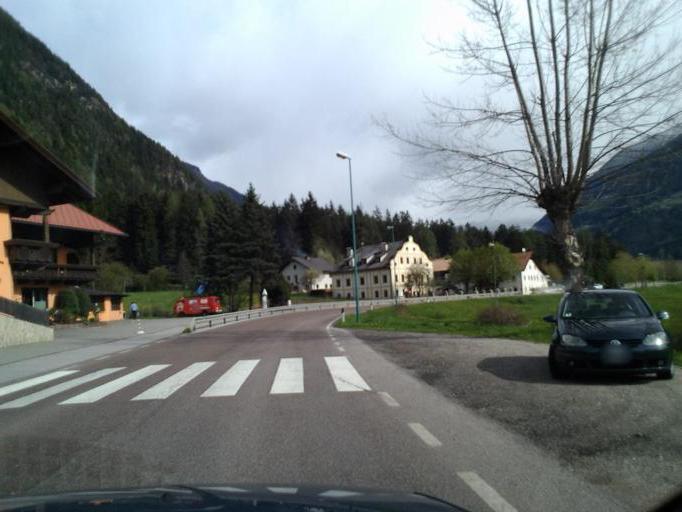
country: IT
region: Trentino-Alto Adige
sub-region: Bolzano
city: Gais
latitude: 46.8417
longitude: 11.9445
